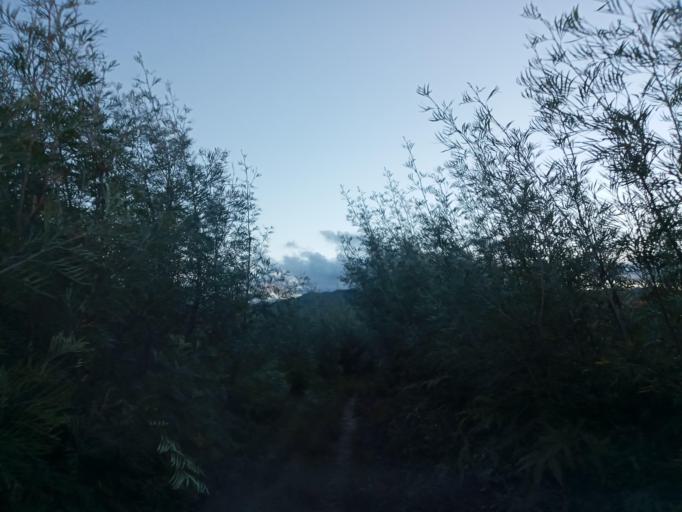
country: MG
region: Anosy
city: Fort Dauphin
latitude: -24.5115
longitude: 47.2236
